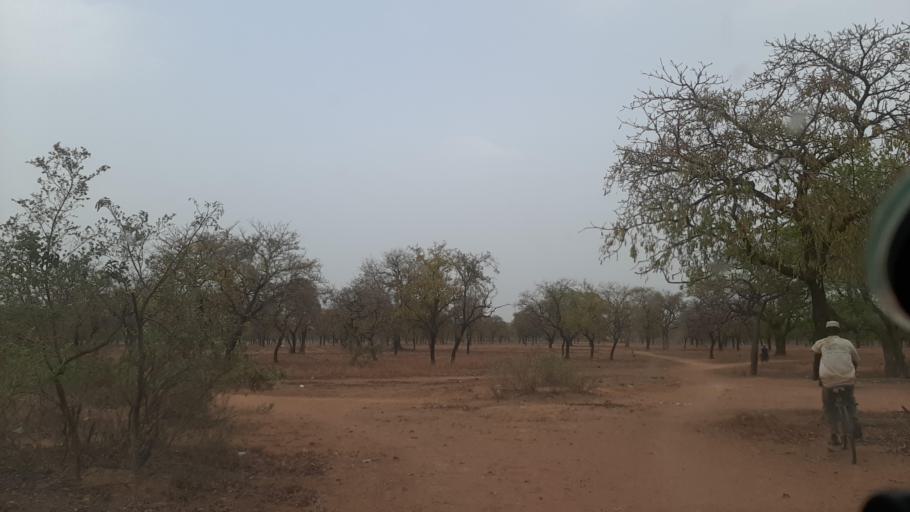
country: BF
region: Boucle du Mouhoun
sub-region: Province des Banwa
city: Salanso
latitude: 11.8690
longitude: -4.4464
